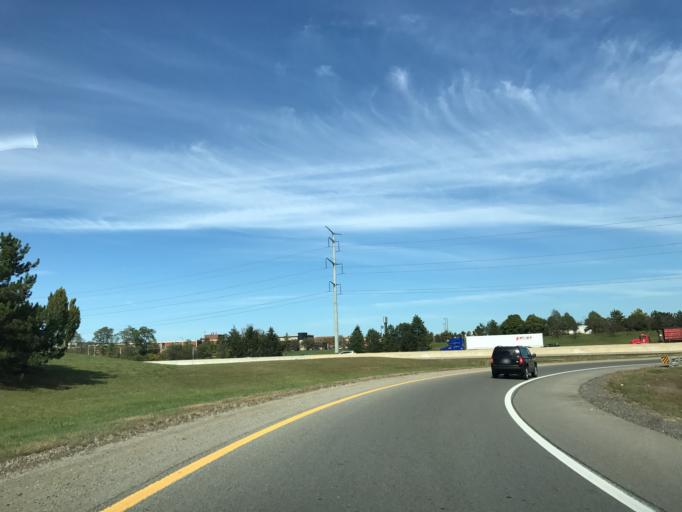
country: US
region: Michigan
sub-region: Oakland County
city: Novi
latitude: 42.4860
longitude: -83.4776
